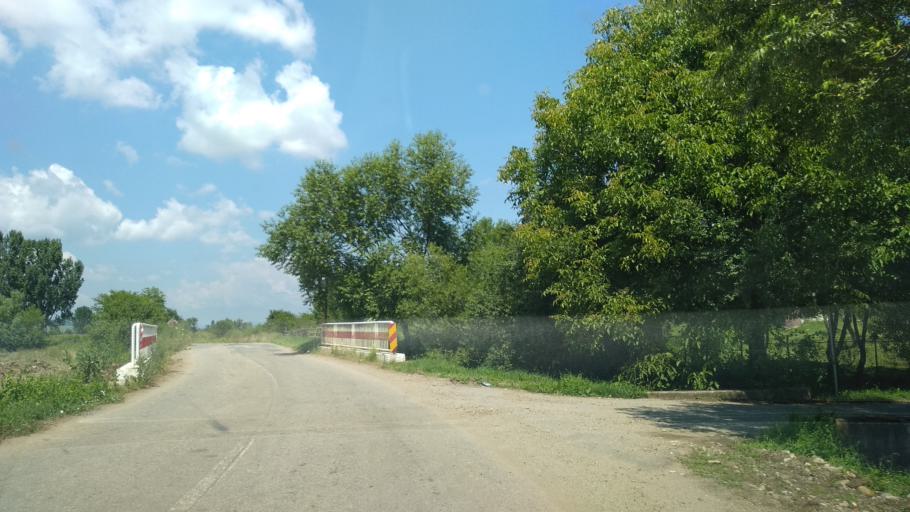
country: RO
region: Hunedoara
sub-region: Comuna Bretea Romana
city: Bretea Romana
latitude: 45.7007
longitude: 23.0173
